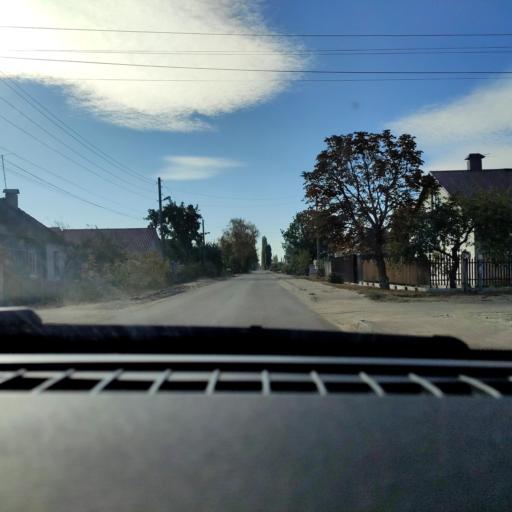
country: RU
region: Voronezj
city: Maslovka
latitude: 51.6083
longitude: 39.2207
